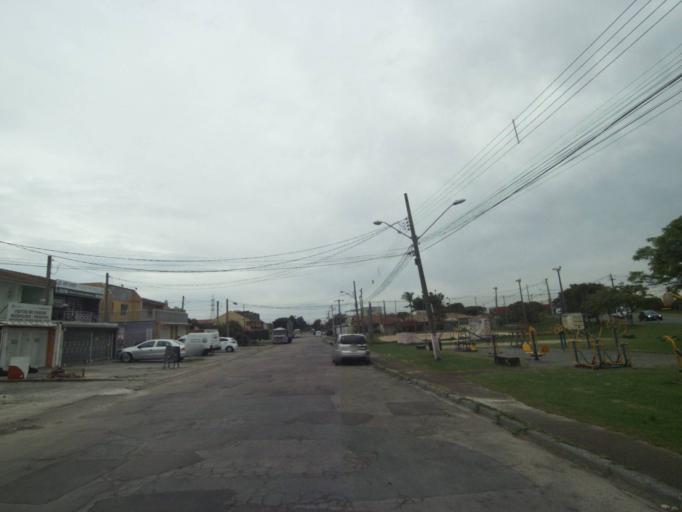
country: BR
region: Parana
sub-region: Pinhais
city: Pinhais
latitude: -25.4281
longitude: -49.2042
